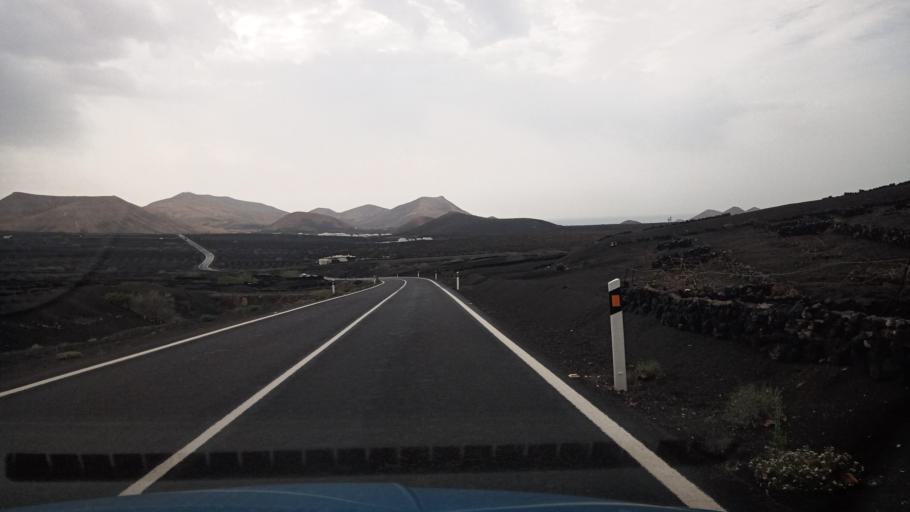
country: ES
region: Canary Islands
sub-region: Provincia de Las Palmas
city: Yaiza
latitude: 28.9640
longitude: -13.7241
